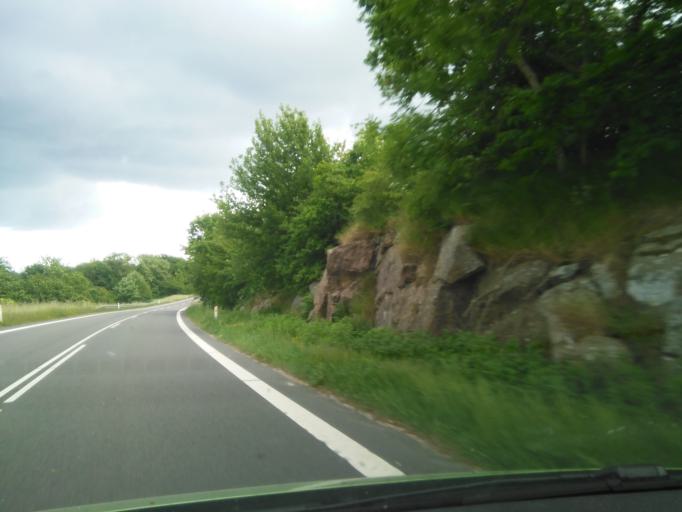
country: DK
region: Capital Region
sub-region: Bornholm Kommune
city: Akirkeby
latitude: 55.2211
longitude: 14.9041
